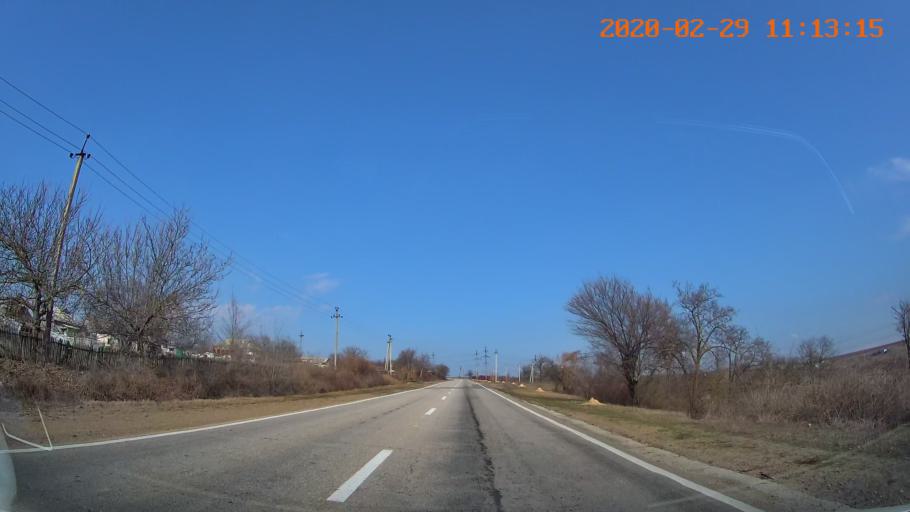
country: MD
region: Telenesti
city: Dubasari
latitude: 47.2701
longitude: 29.1815
